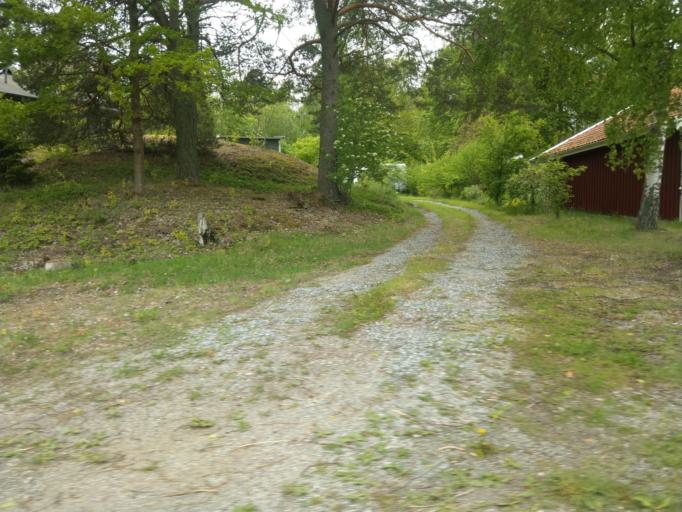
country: SE
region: Stockholm
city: Stenhamra
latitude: 59.4087
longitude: 17.6234
